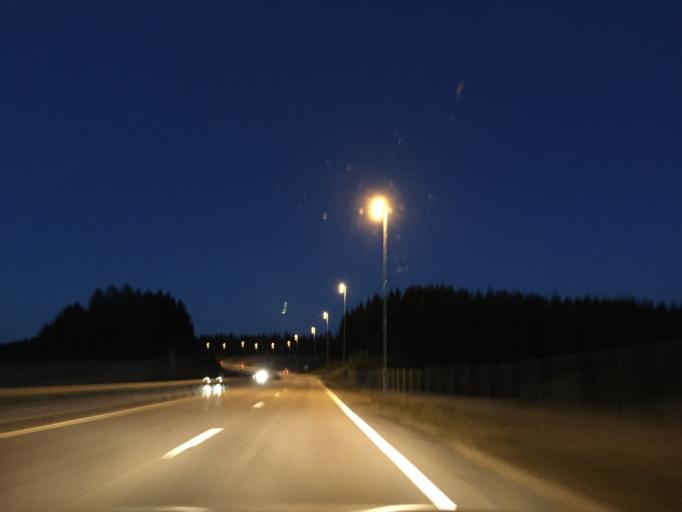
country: NO
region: Akershus
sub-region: Ullensaker
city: Jessheim
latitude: 60.0946
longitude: 11.2416
